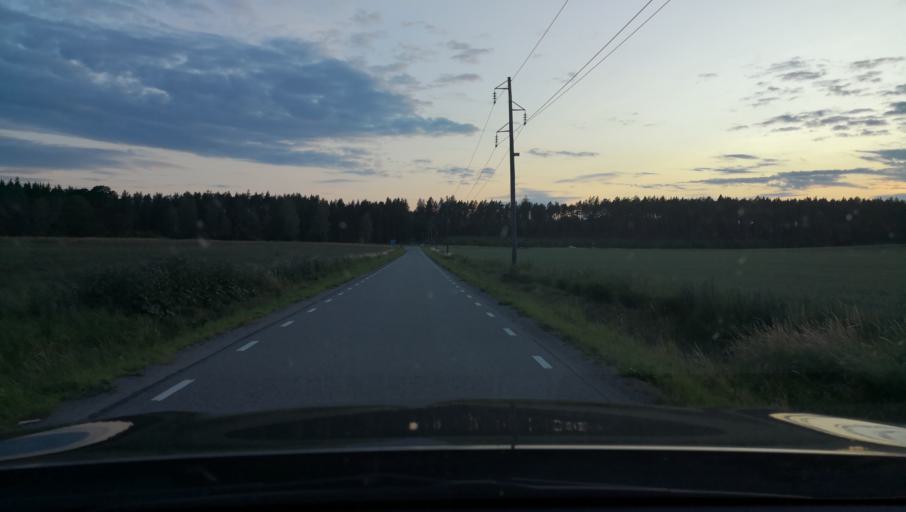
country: SE
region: Uppsala
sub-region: Osthammars Kommun
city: Bjorklinge
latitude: 60.0626
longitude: 17.5504
